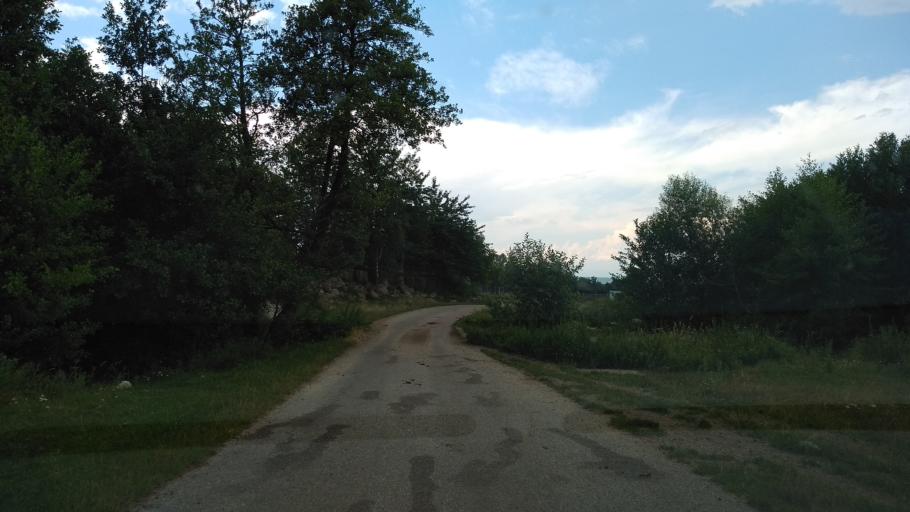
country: RO
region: Hunedoara
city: Salasu de Sus
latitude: 45.4875
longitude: 22.9644
